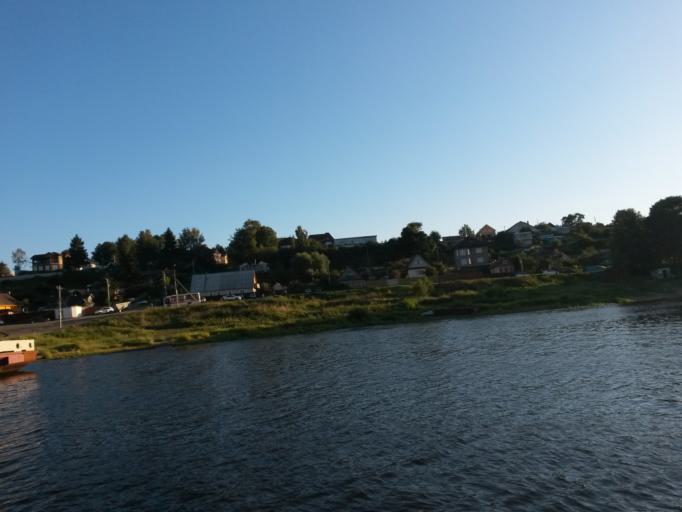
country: RU
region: Jaroslavl
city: Tutayev
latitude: 57.8748
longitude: 39.5362
